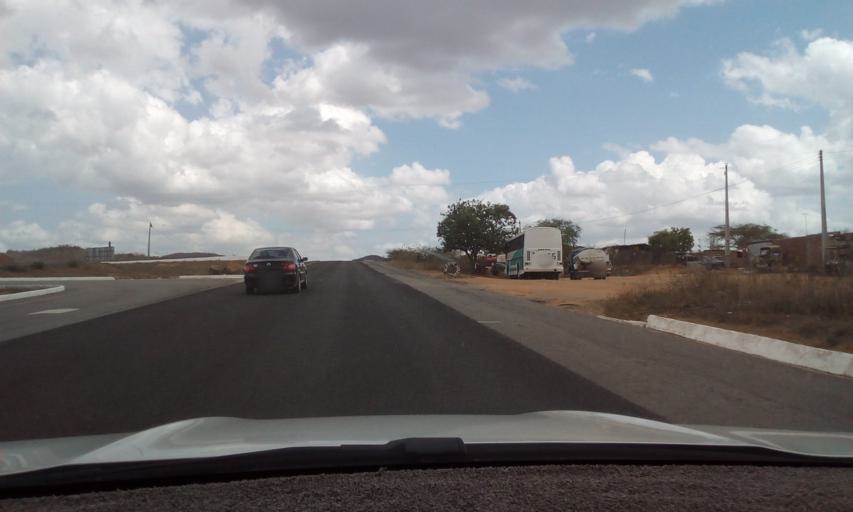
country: BR
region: Pernambuco
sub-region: Toritama
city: Toritama
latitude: -8.1101
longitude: -36.0188
